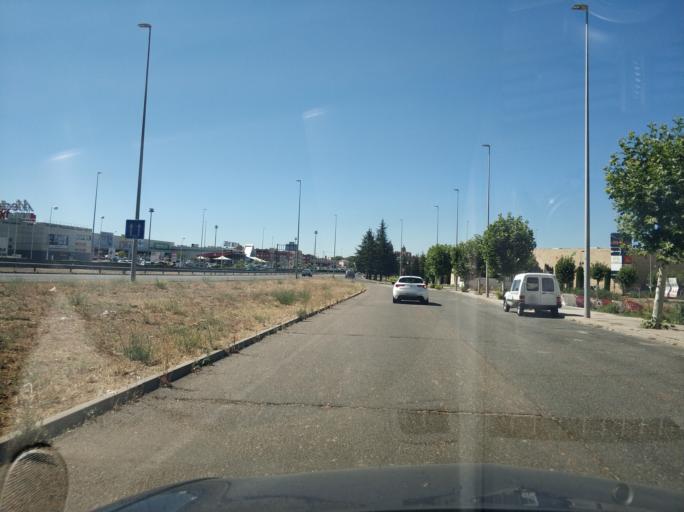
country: ES
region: Castille and Leon
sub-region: Provincia de Salamanca
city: Carbajosa de la Sagrada
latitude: 40.9483
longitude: -5.6480
